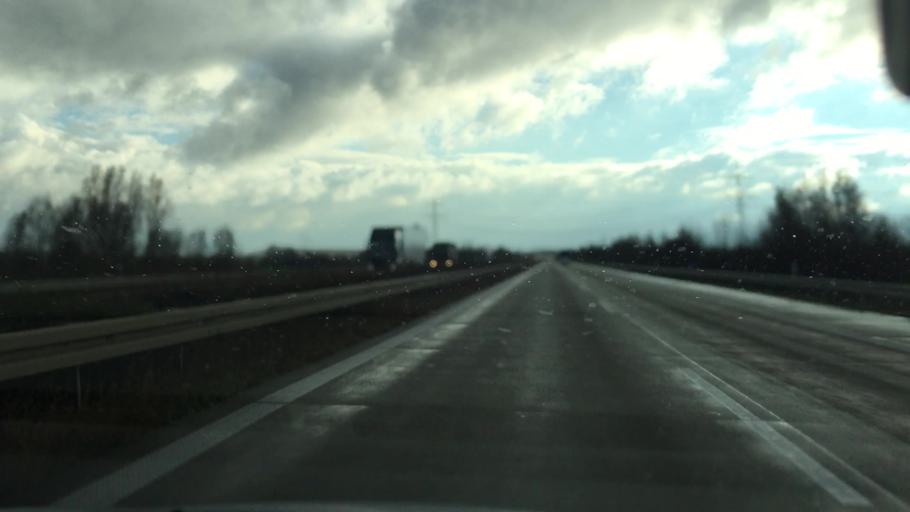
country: DE
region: Saxony-Anhalt
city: Biere
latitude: 51.9867
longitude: 11.6669
